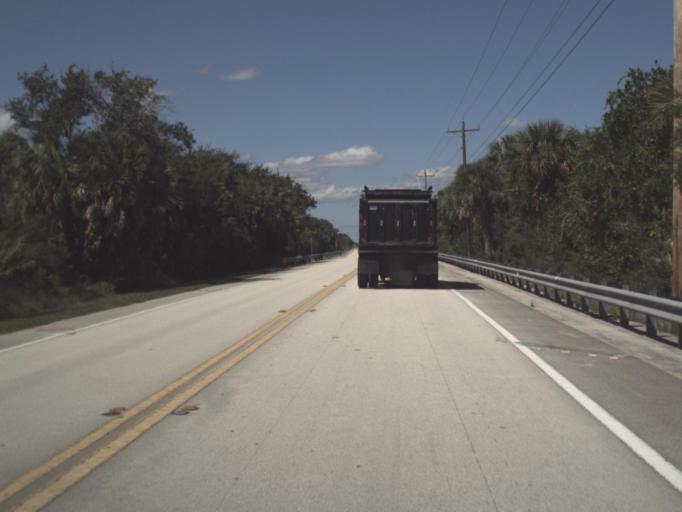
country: US
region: Florida
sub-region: Collier County
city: Marco
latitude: 25.9659
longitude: -81.5298
